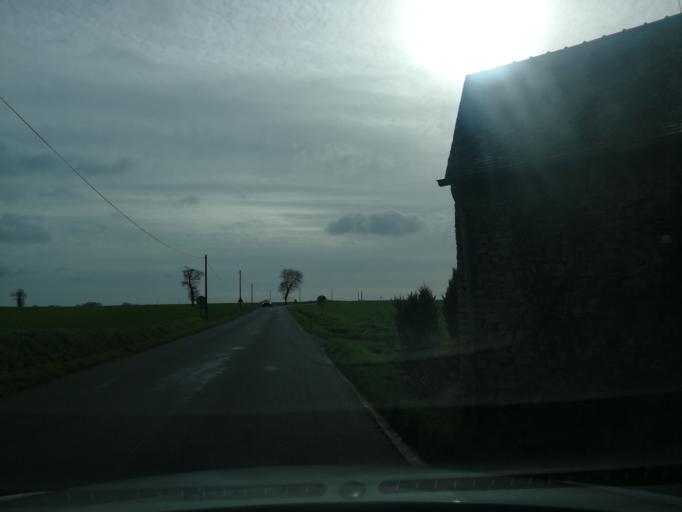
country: FR
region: Brittany
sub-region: Departement d'Ille-et-Vilaine
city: Bourg-des-Comptes
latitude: 47.9129
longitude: -1.7069
